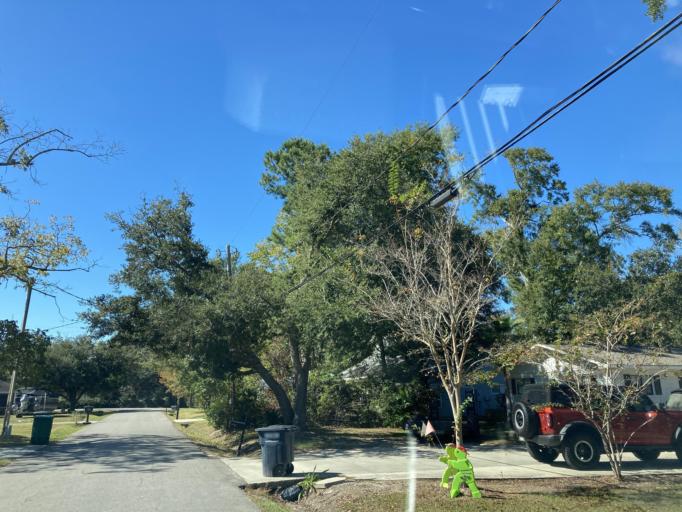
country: US
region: Mississippi
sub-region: Jackson County
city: Ocean Springs
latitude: 30.4092
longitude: -88.8152
